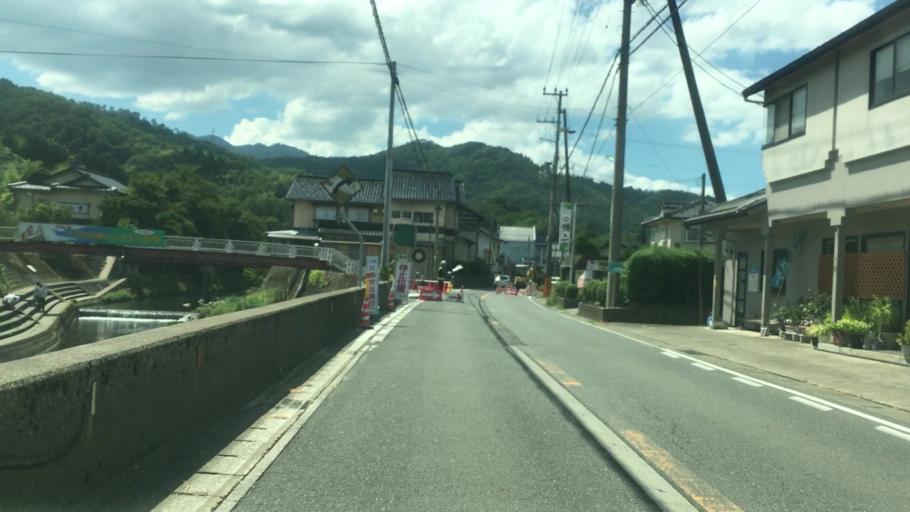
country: JP
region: Hyogo
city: Toyooka
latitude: 35.4721
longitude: 134.7180
